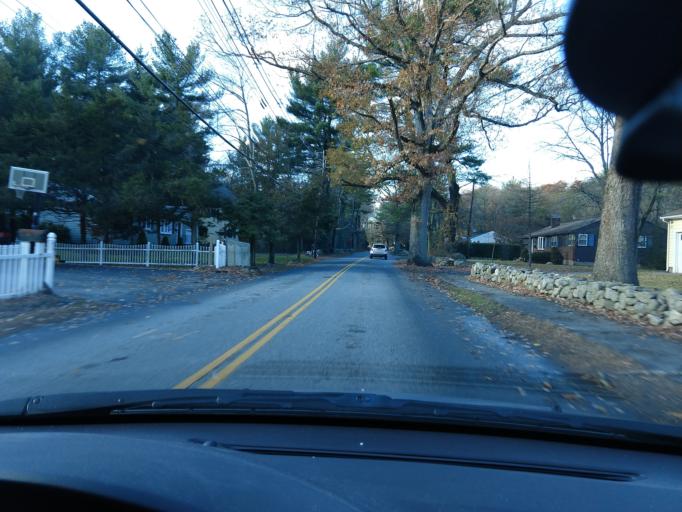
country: US
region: Massachusetts
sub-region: Middlesex County
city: Bedford
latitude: 42.4933
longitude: -71.2648
